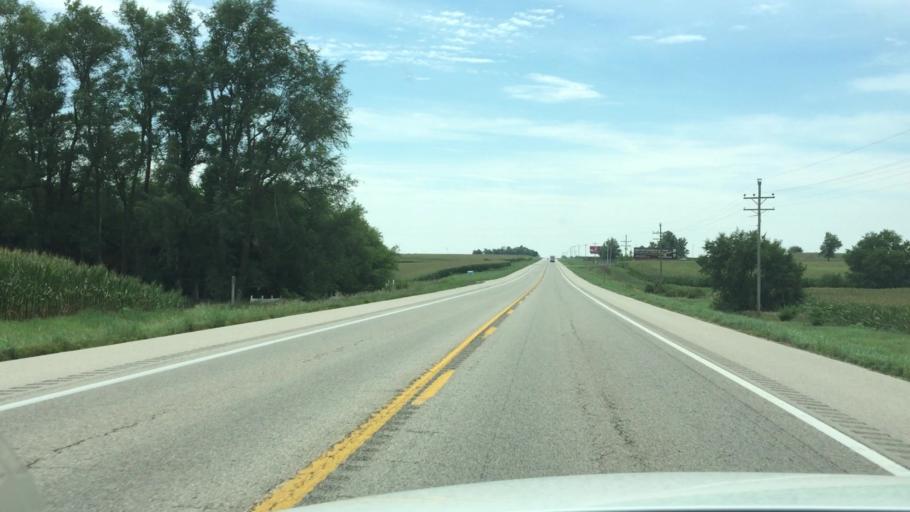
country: US
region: Kansas
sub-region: Nemaha County
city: Sabetha
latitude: 39.7630
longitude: -95.7296
